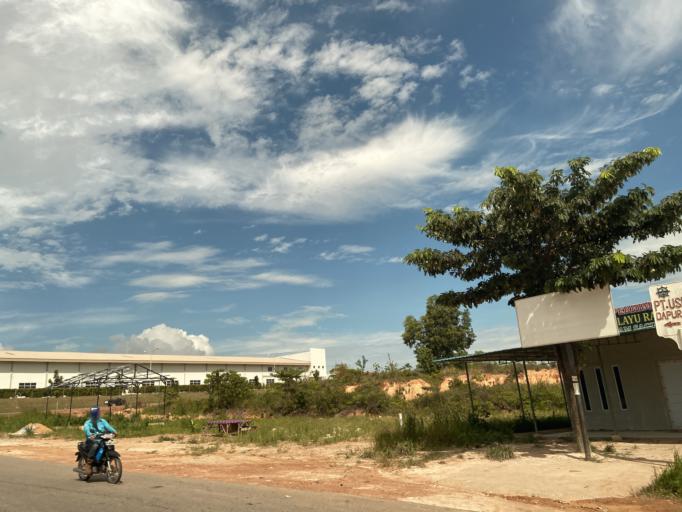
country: SG
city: Singapore
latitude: 1.0227
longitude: 103.9457
